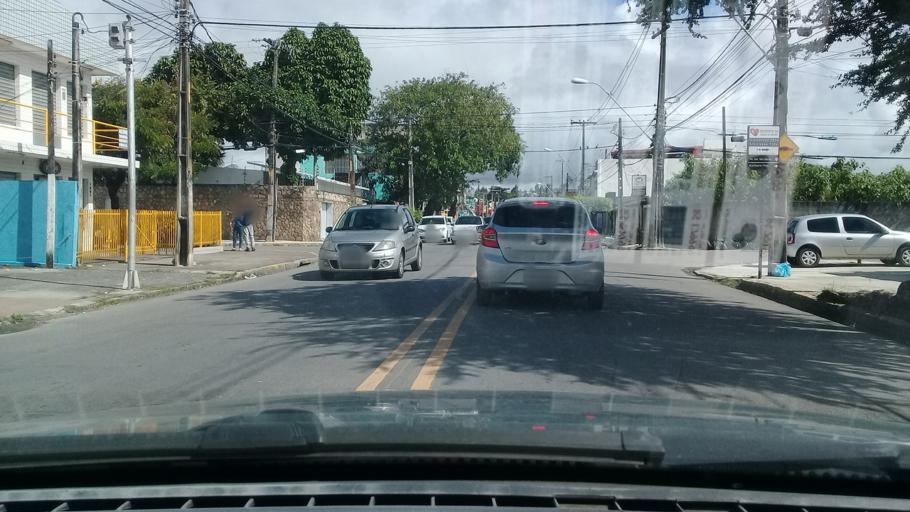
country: BR
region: Pernambuco
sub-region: Recife
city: Recife
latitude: -8.0675
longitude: -34.9279
